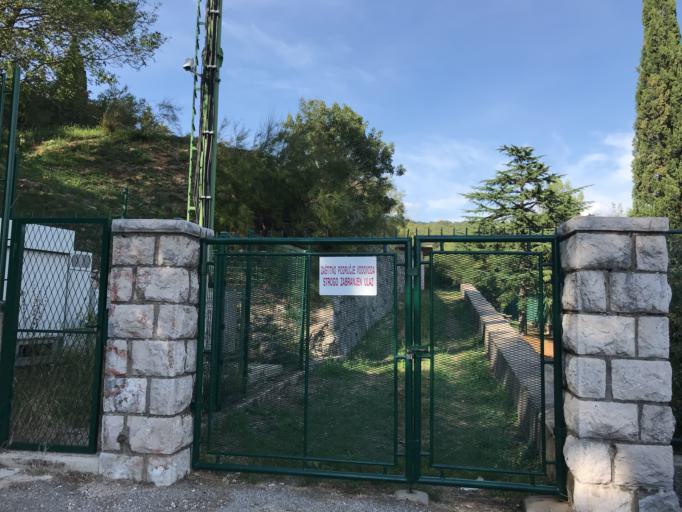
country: HR
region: Primorsko-Goranska
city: Drenova
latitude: 45.3317
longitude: 14.4494
